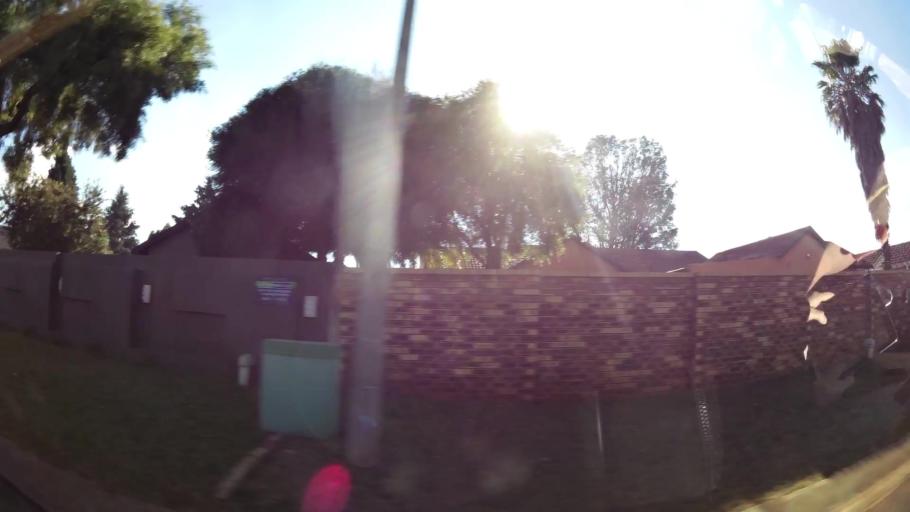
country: ZA
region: Gauteng
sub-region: City of Johannesburg Metropolitan Municipality
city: Roodepoort
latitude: -26.1607
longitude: 27.8223
